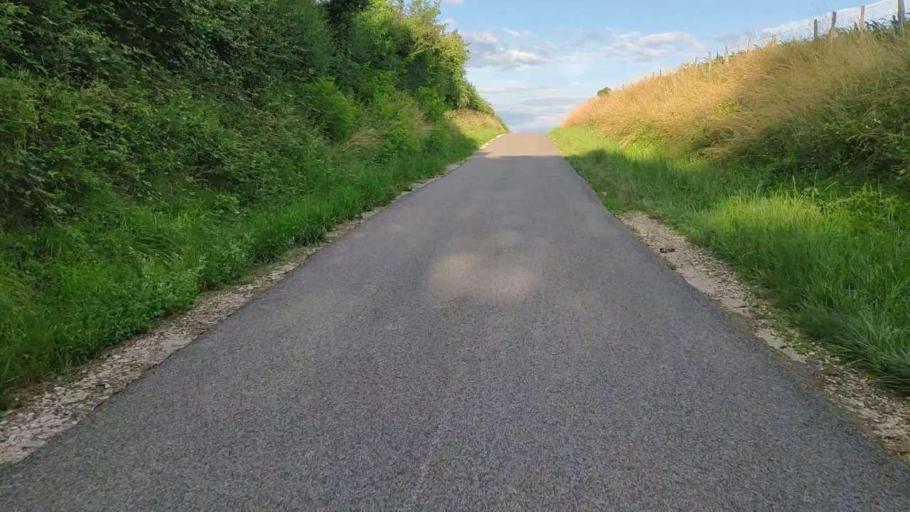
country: FR
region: Franche-Comte
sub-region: Departement du Jura
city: Bletterans
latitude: 46.7823
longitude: 5.5006
